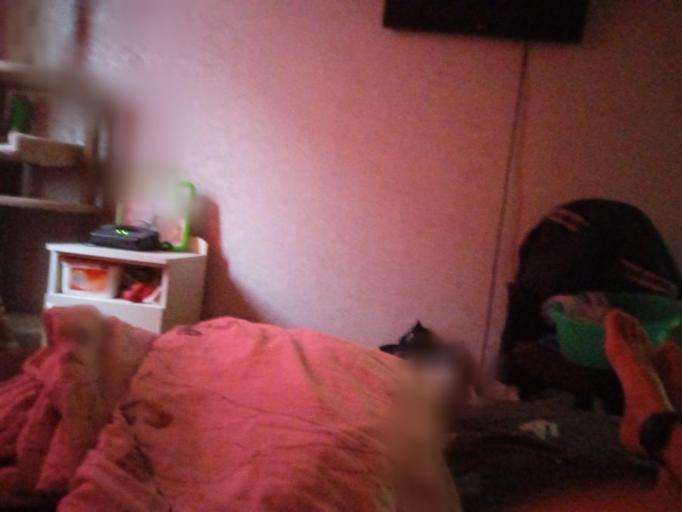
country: RU
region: Saratov
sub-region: Saratovskiy Rayon
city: Saratov
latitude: 51.6249
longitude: 45.9781
